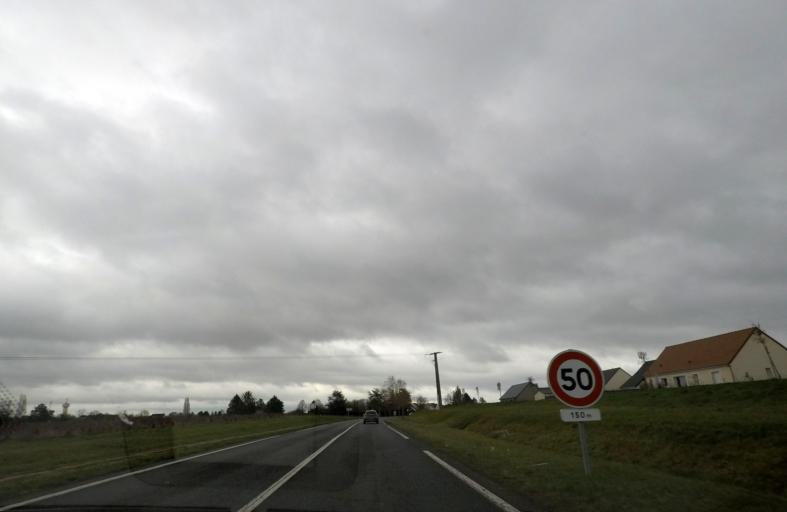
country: FR
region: Centre
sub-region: Departement du Loir-et-Cher
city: Cour-Cheverny
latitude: 47.5165
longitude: 1.4516
